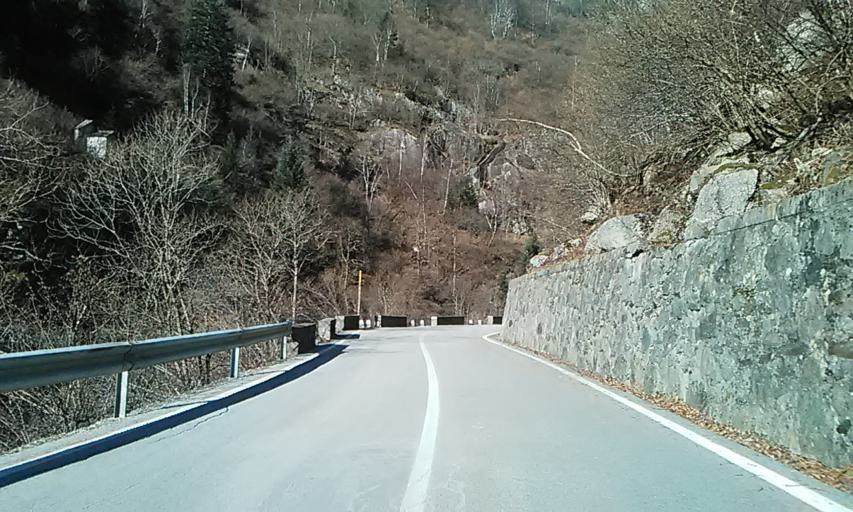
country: IT
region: Piedmont
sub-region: Provincia di Vercelli
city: Rimasco
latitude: 45.8451
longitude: 8.0667
